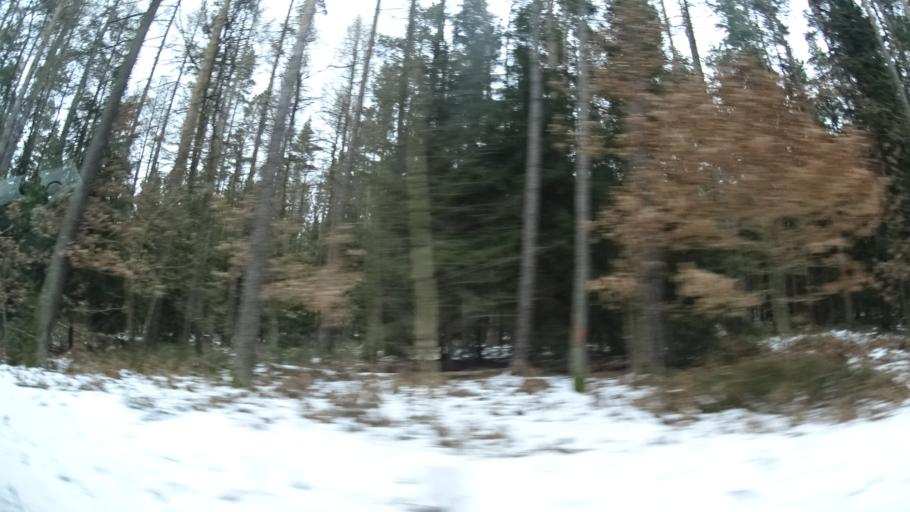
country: DE
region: Thuringia
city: Langewiesen
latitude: 50.6882
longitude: 10.9616
